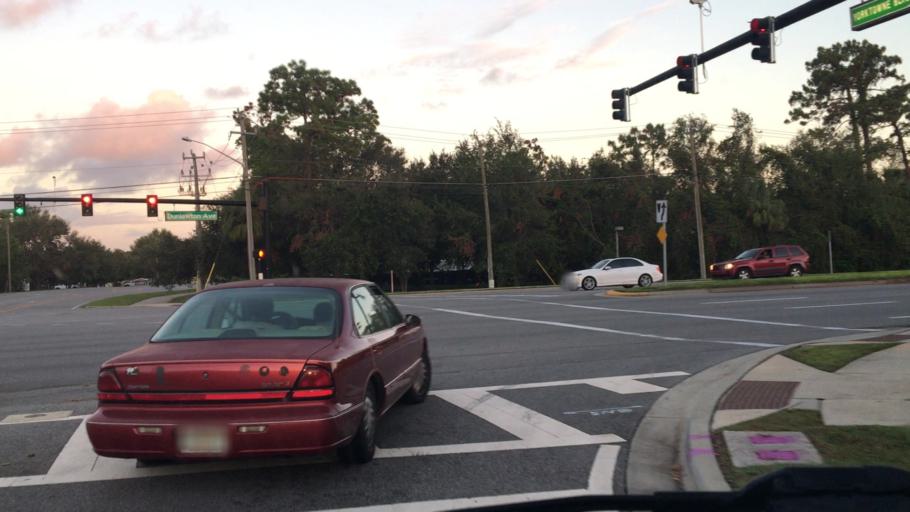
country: US
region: Florida
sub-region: Volusia County
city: Port Orange
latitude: 29.1124
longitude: -81.0251
